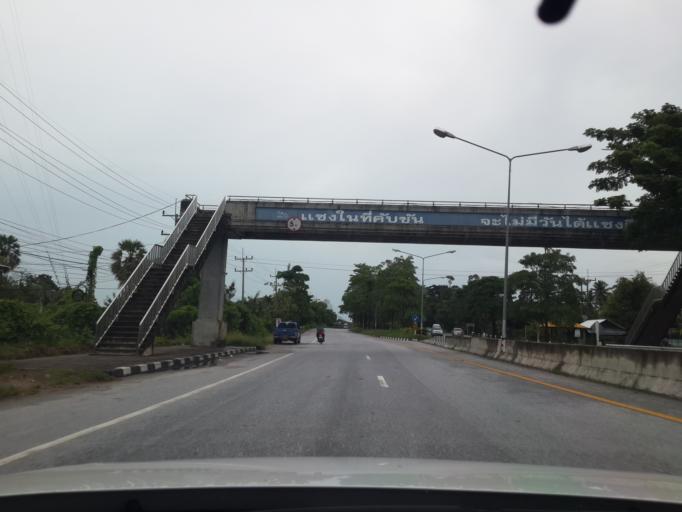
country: TH
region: Songkhla
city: Chana
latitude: 6.9482
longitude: 100.8311
